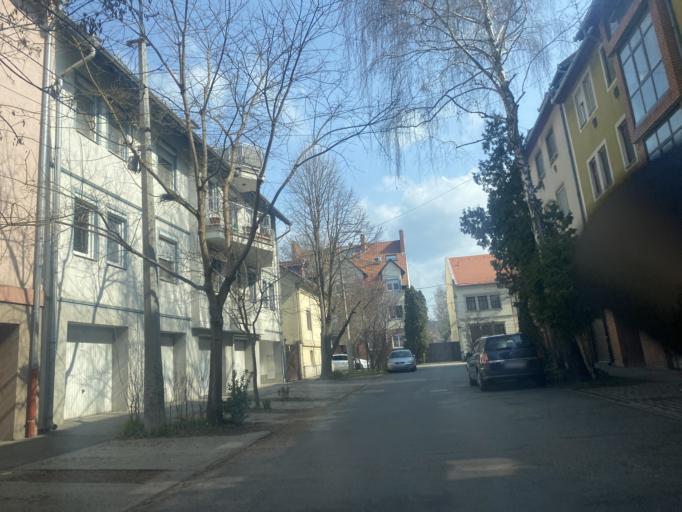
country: HU
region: Csongrad
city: Szeged
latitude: 46.2628
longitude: 20.1538
